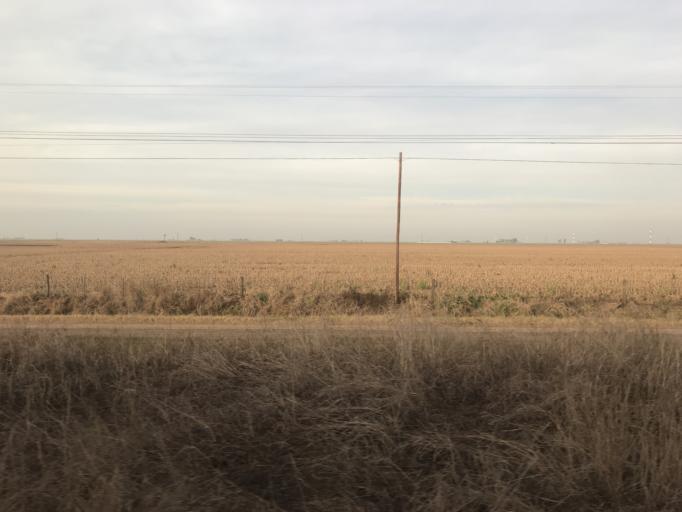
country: AR
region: Cordoba
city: Marcos Juarez
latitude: -32.6853
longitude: -62.1829
